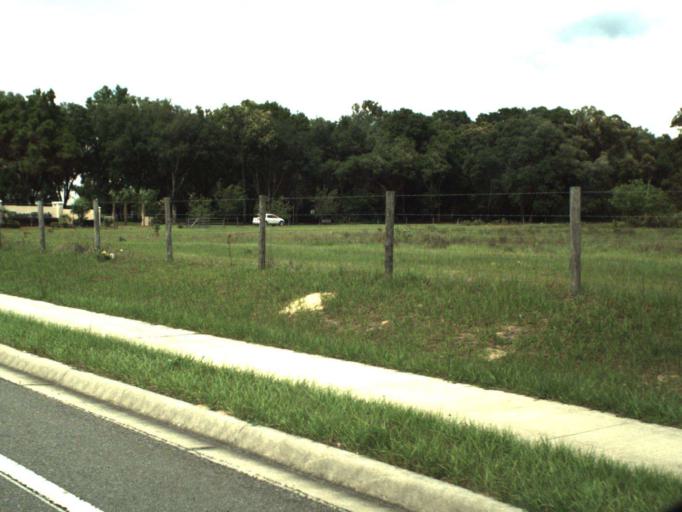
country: US
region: Florida
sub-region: Marion County
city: Silver Springs Shores
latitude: 29.1779
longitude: -82.0535
